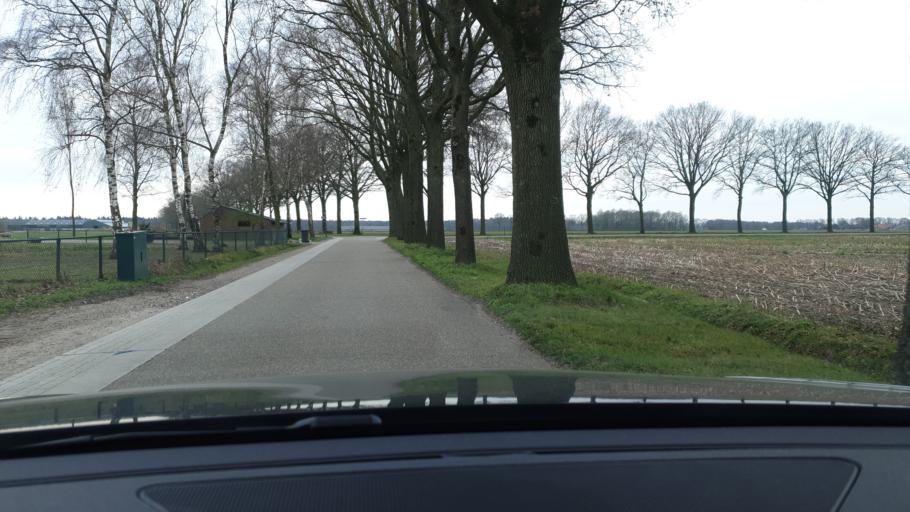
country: NL
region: North Brabant
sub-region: Gemeente Veldhoven
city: Oerle
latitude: 51.4104
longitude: 5.3295
